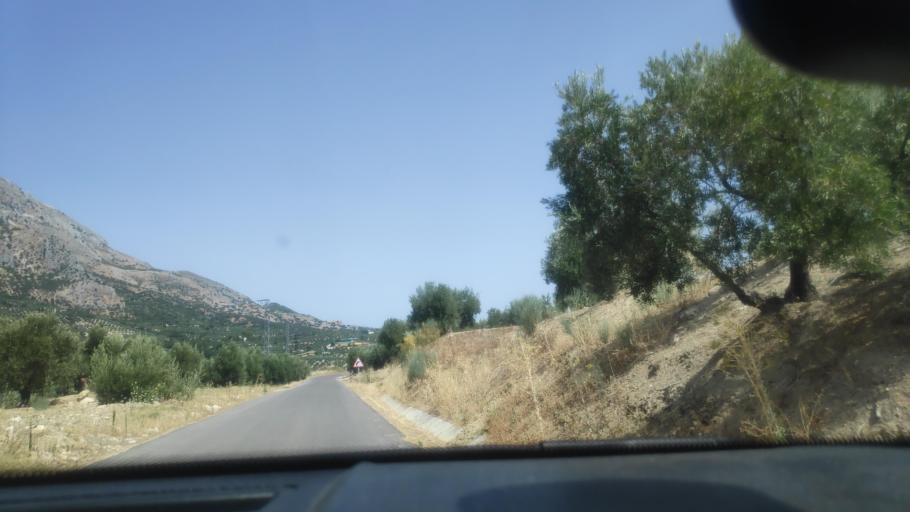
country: ES
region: Andalusia
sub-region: Provincia de Jaen
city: Jimena
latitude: 37.7981
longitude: -3.4488
